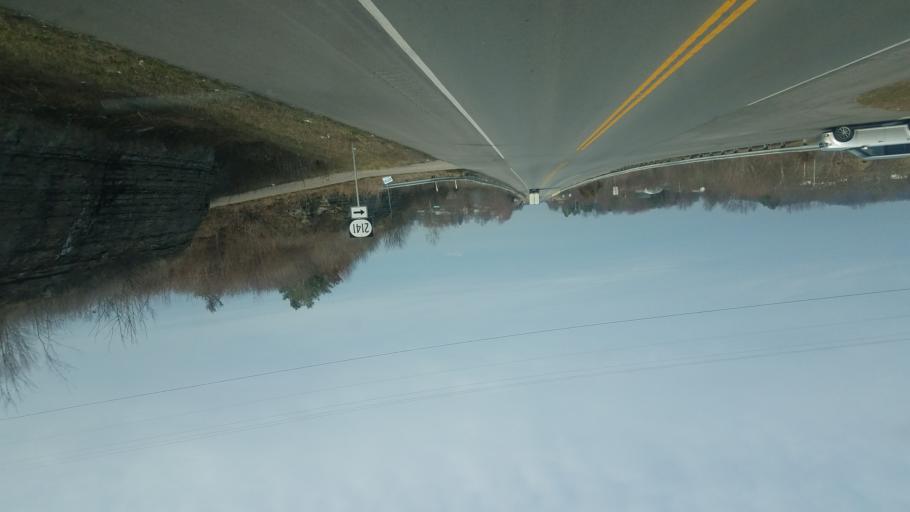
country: US
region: Kentucky
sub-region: Boyle County
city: Junction City
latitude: 37.5376
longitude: -84.8039
